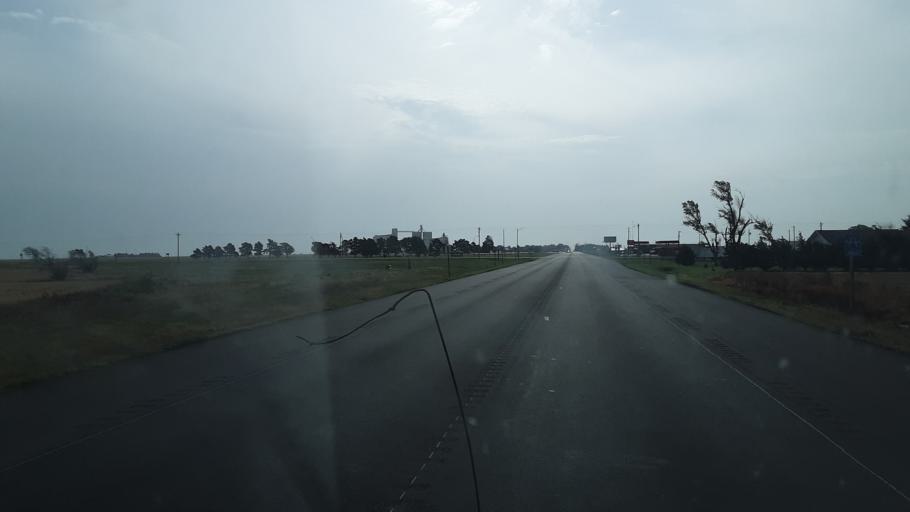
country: US
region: Kansas
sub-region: Ford County
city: Dodge City
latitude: 37.7789
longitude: -99.9086
